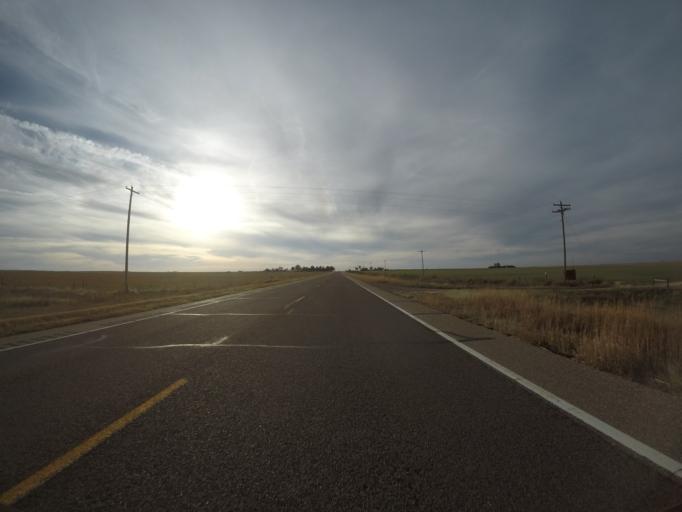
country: US
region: Colorado
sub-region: Kit Carson County
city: Burlington
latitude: 39.6581
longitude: -102.5268
